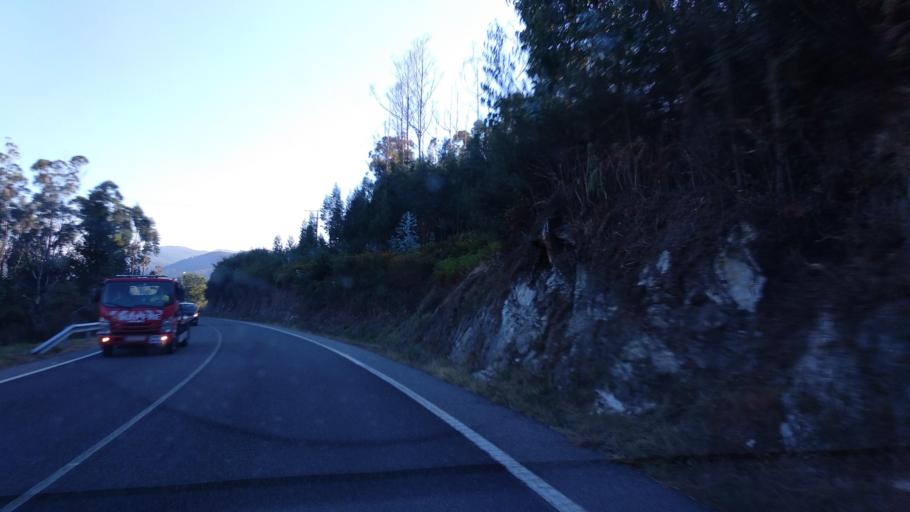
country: ES
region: Galicia
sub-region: Provincia de Pontevedra
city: Ponte Caldelas
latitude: 42.3590
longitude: -8.5413
